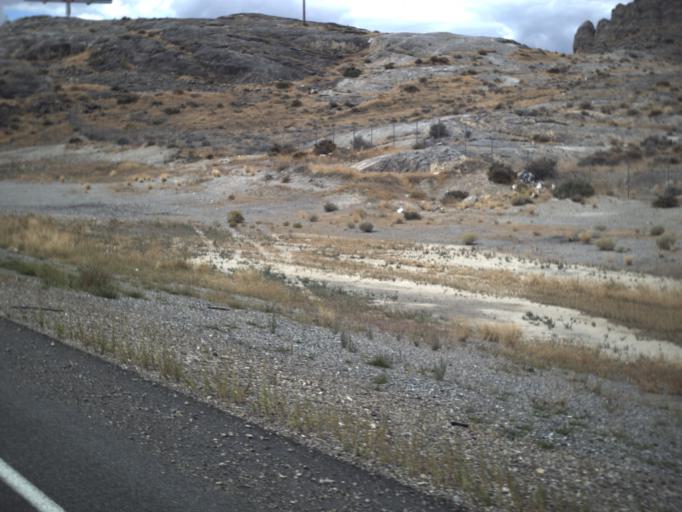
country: US
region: Utah
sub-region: Tooele County
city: Wendover
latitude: 40.7390
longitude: -114.0391
